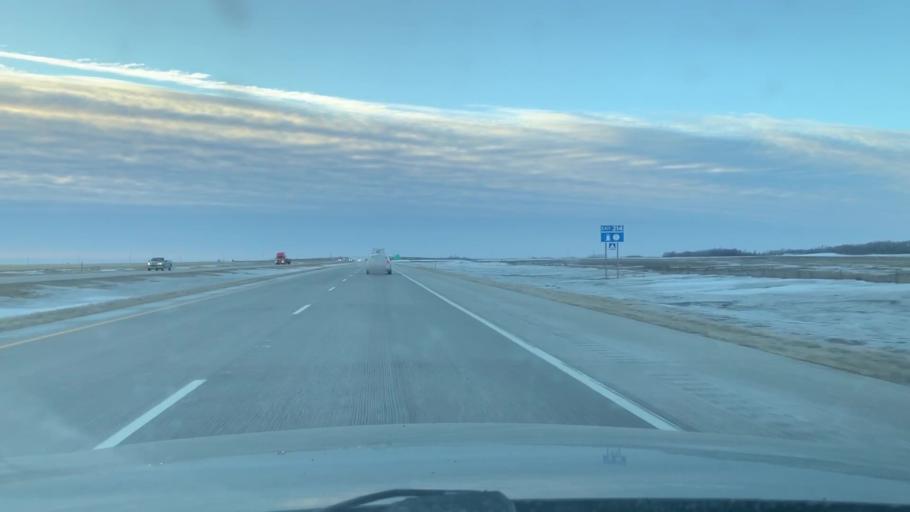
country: US
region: North Dakota
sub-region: Ransom County
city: Sheldon
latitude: 46.8758
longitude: -97.5376
